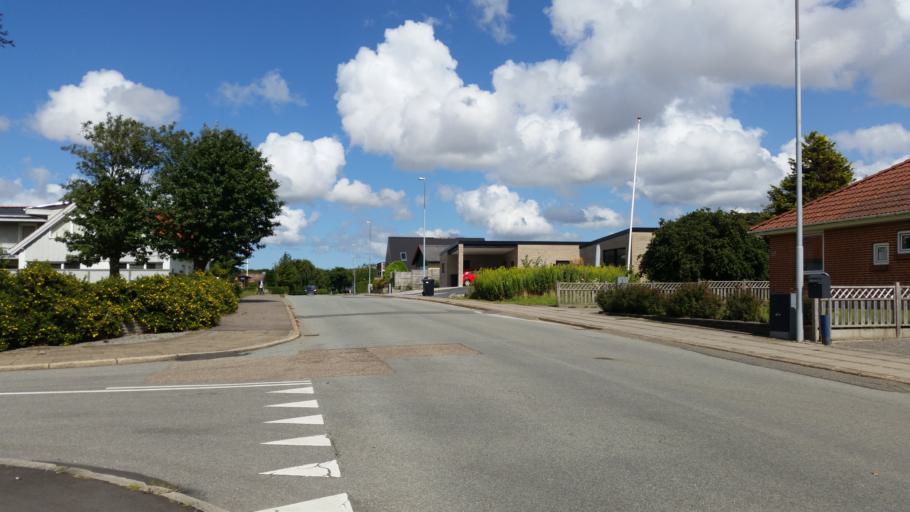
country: DK
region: North Denmark
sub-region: Thisted Kommune
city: Thisted
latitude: 56.9593
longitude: 8.6978
